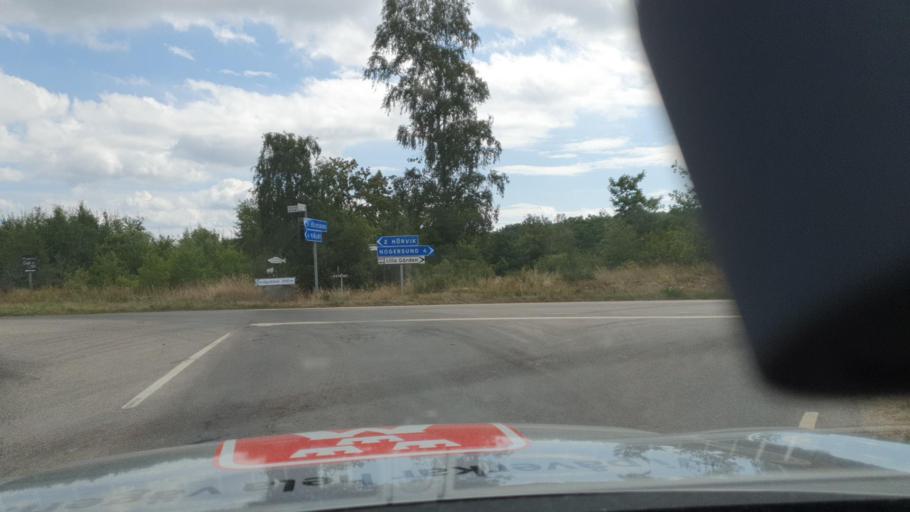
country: SE
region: Blekinge
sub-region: Karlshamns Kommun
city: Morrum
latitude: 56.0365
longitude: 14.7338
